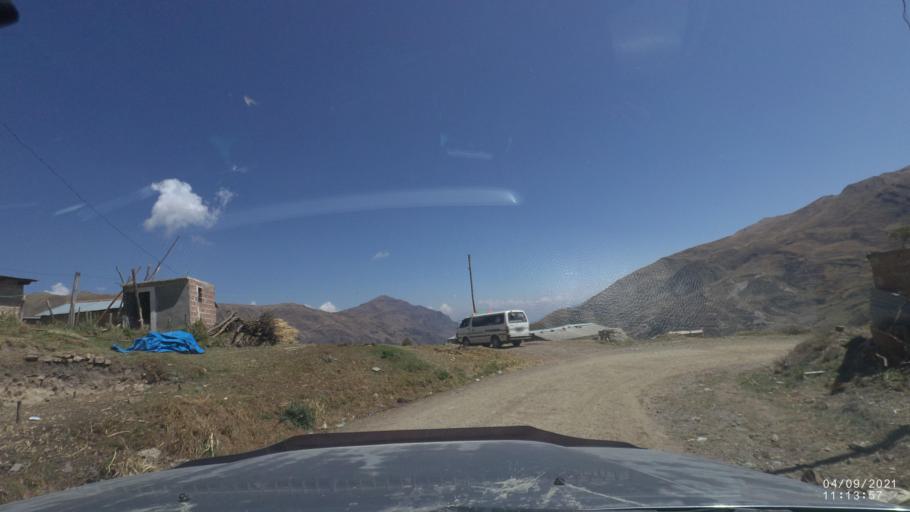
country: BO
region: Cochabamba
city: Sipe Sipe
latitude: -17.2723
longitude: -66.4919
